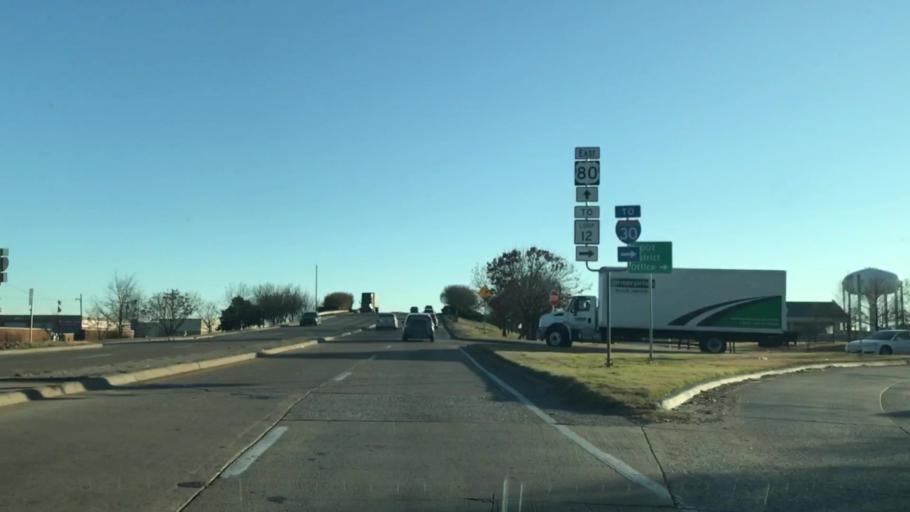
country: US
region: Texas
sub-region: Dallas County
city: Mesquite
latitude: 32.7993
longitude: -96.6683
